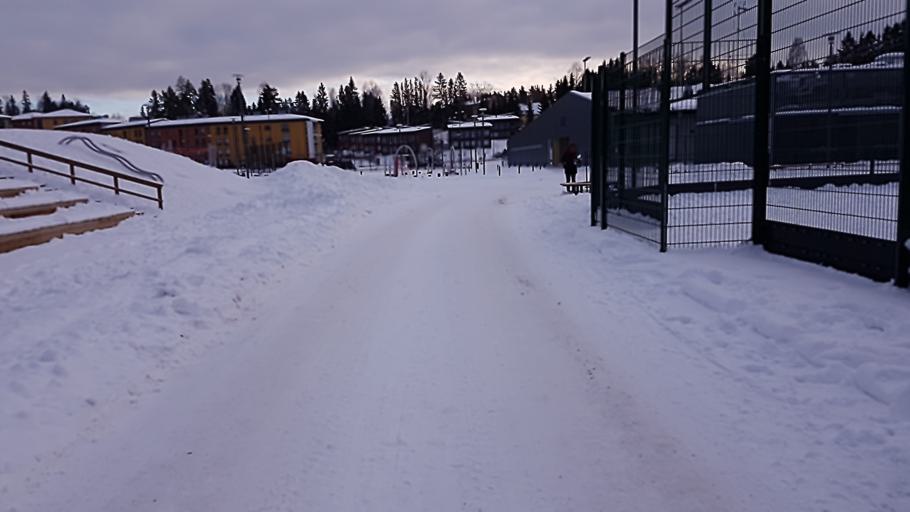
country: FI
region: Uusimaa
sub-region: Helsinki
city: Espoo
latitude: 60.2105
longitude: 24.6744
